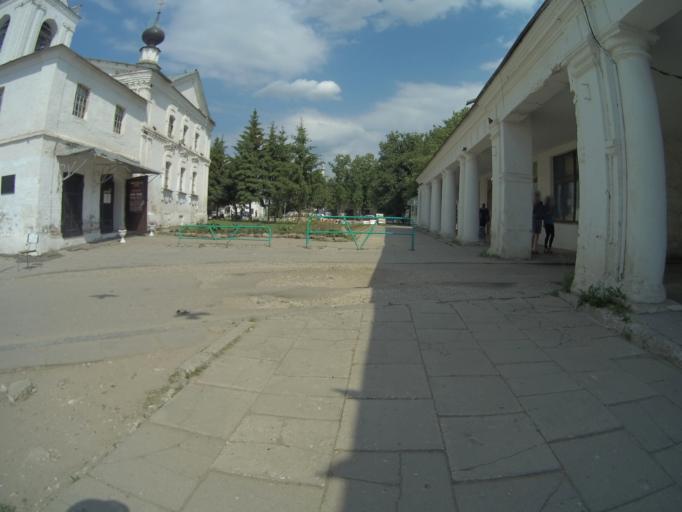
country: RU
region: Vladimir
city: Suzdal'
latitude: 56.4211
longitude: 40.4476
